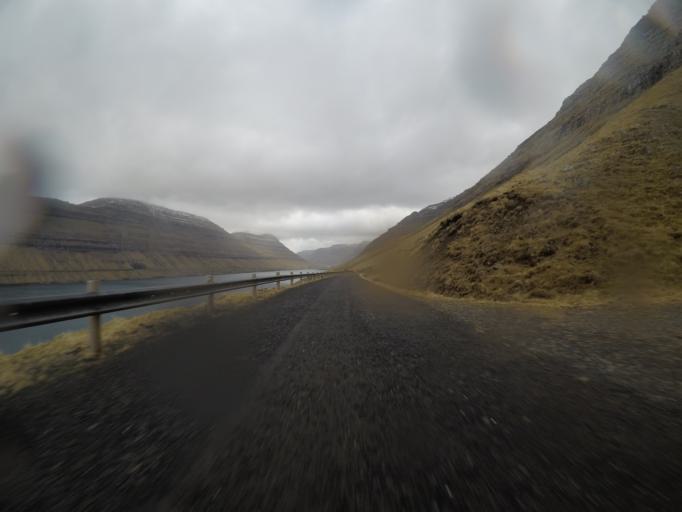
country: FO
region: Nordoyar
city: Klaksvik
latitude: 62.3286
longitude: -6.5689
